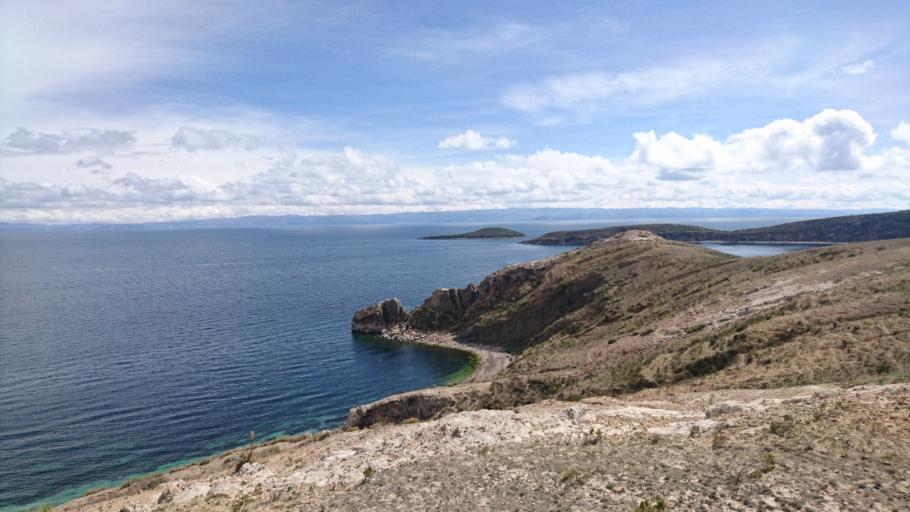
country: BO
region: La Paz
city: Yumani
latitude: -15.9878
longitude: -69.2047
